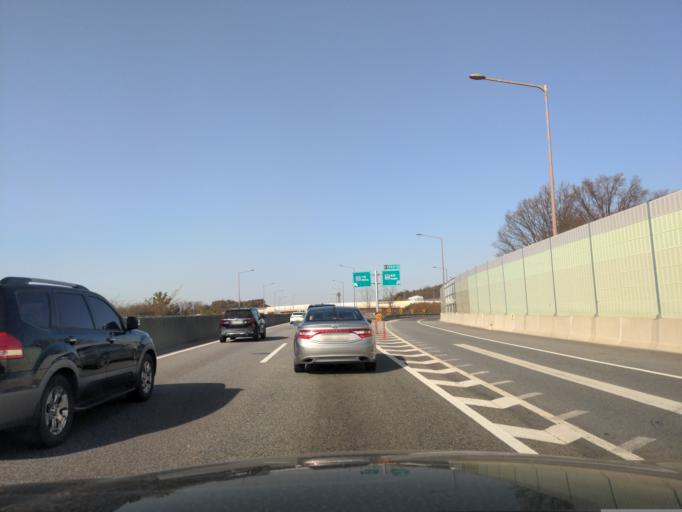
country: KR
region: Gyeonggi-do
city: Hwaseong-si
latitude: 37.1843
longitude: 126.7781
